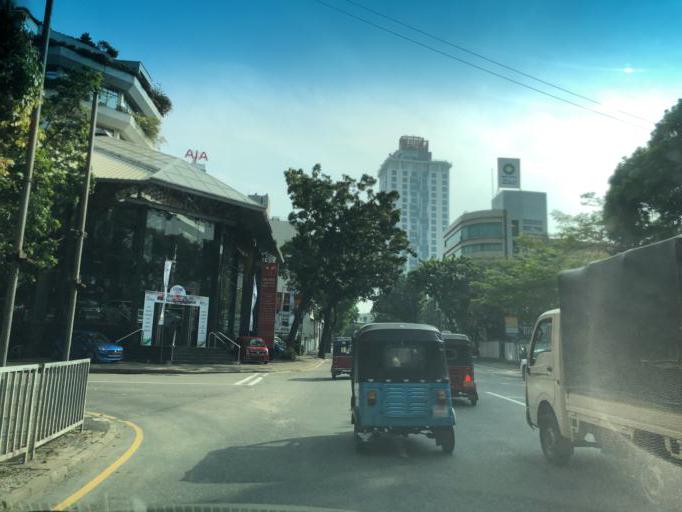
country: LK
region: Western
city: Colombo
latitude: 6.9147
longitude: 79.8560
